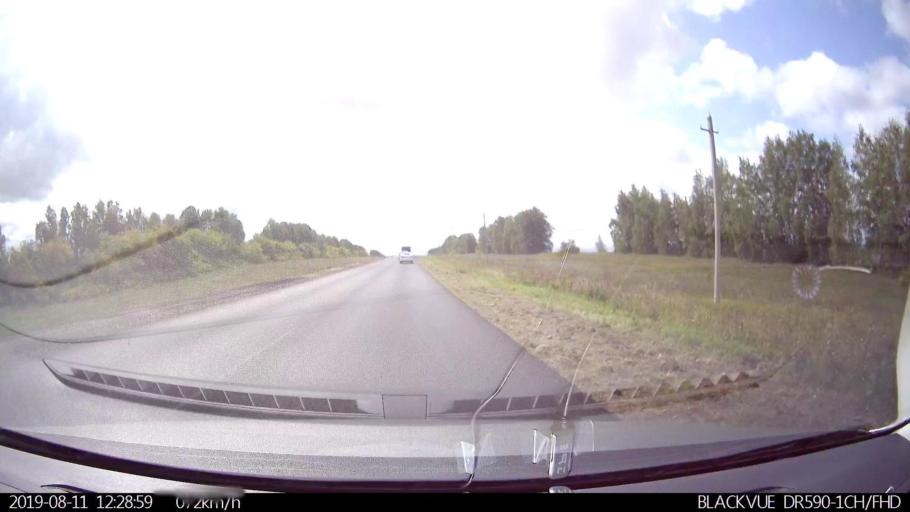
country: RU
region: Ulyanovsk
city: Ignatovka
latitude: 53.8390
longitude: 47.9065
